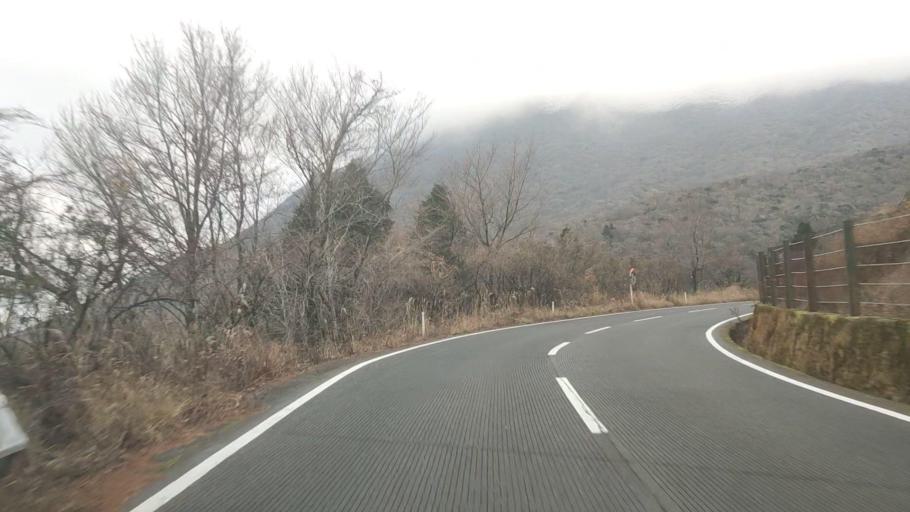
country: JP
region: Nagasaki
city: Shimabara
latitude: 32.7647
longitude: 130.2734
